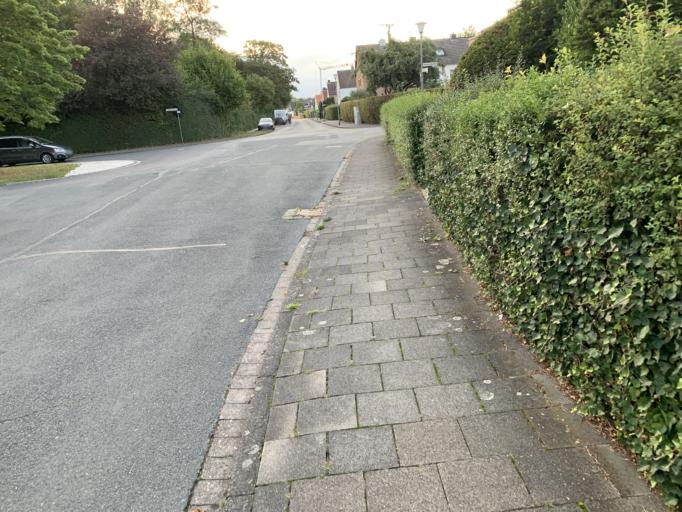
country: DE
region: North Rhine-Westphalia
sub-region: Regierungsbezirk Munster
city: Muenster
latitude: 51.9399
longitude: 7.6021
